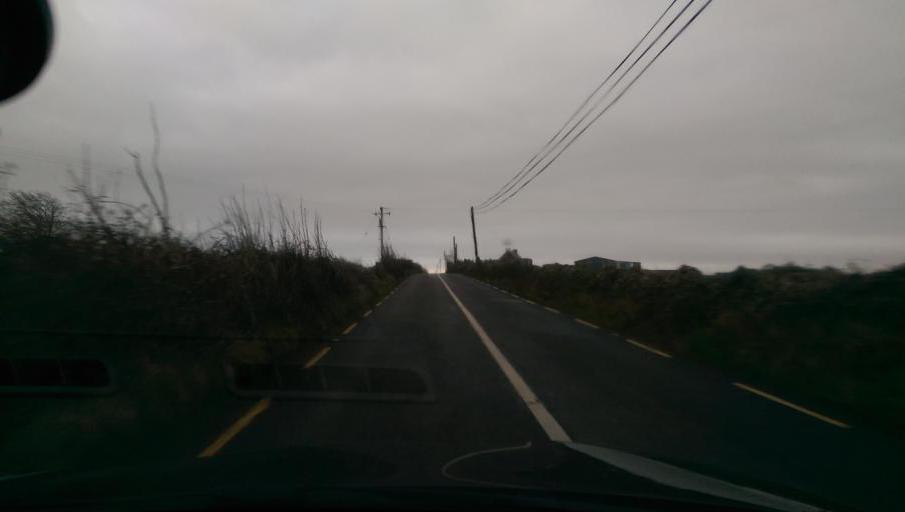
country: IE
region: Connaught
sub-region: County Galway
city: Athenry
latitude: 53.3133
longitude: -8.8034
